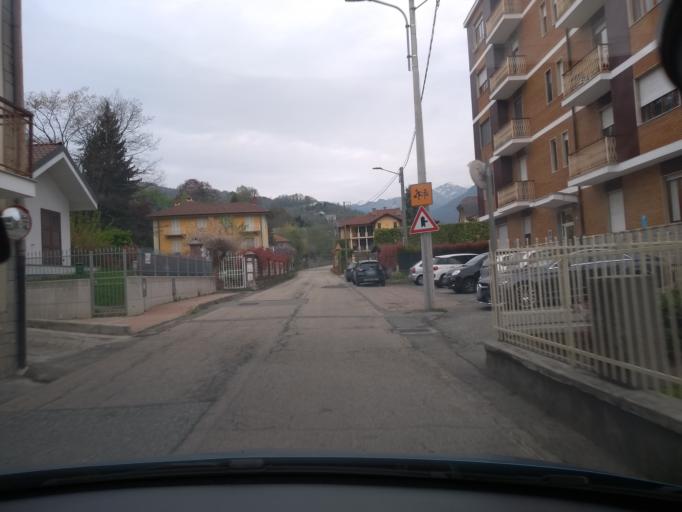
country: IT
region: Piedmont
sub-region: Provincia di Torino
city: Lanzo Torinese
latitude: 45.2762
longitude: 7.4720
